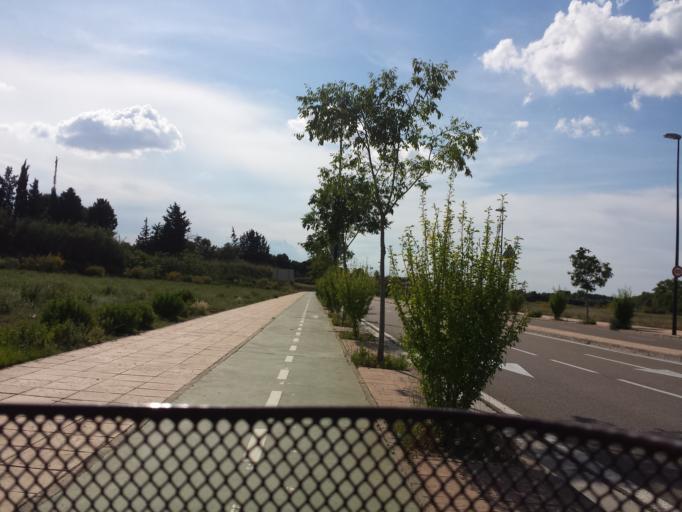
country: ES
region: Aragon
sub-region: Provincia de Zaragoza
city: Montecanal
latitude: 41.6326
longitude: -0.9310
